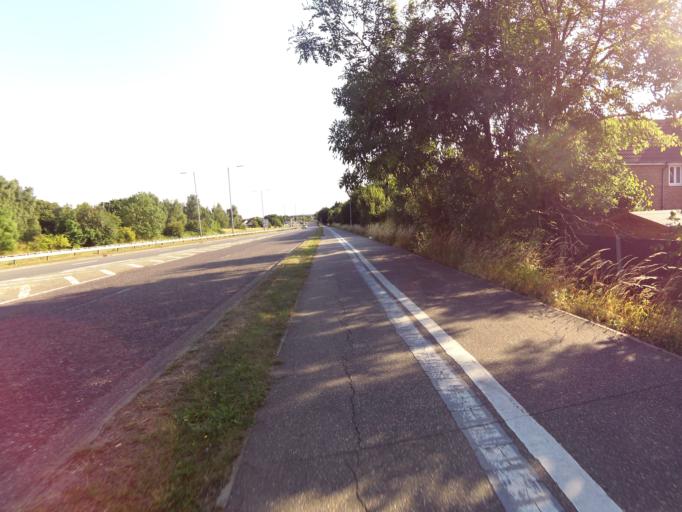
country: GB
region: England
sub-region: Essex
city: Chelmsford
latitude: 51.7430
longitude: 0.4993
